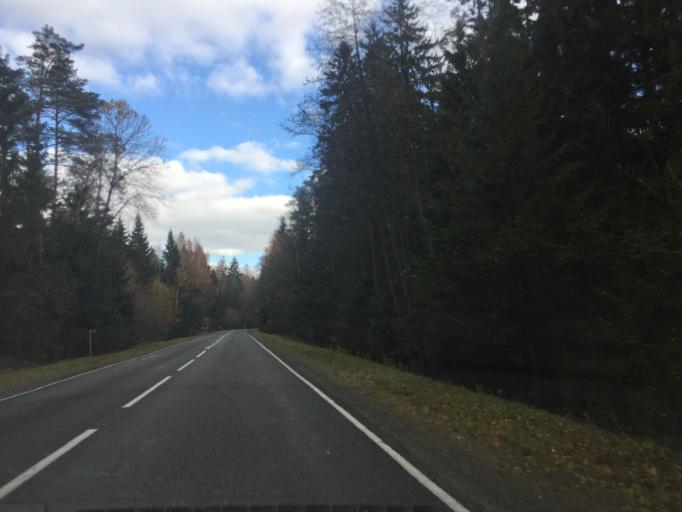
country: BY
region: Minsk
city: Svir
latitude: 54.9267
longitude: 26.5418
